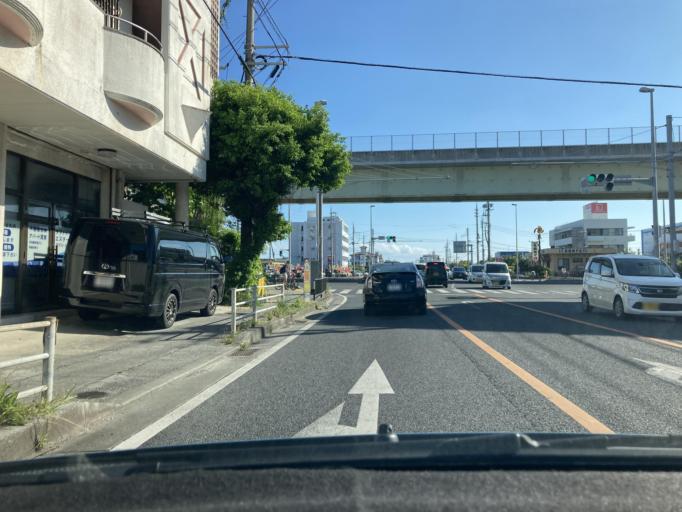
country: JP
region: Okinawa
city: Tomigusuku
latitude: 26.1756
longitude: 127.6657
